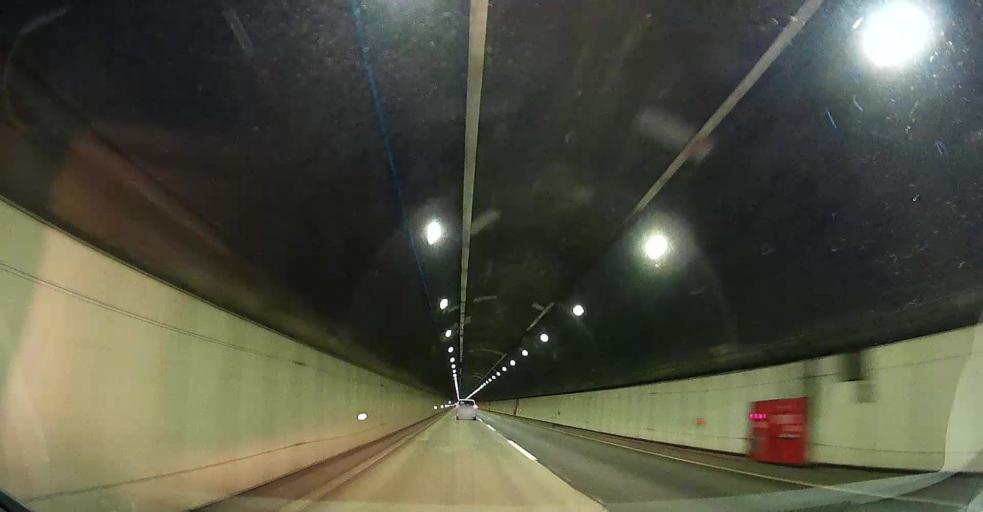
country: JP
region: Kanagawa
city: Ninomiya
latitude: 35.2932
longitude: 139.2064
